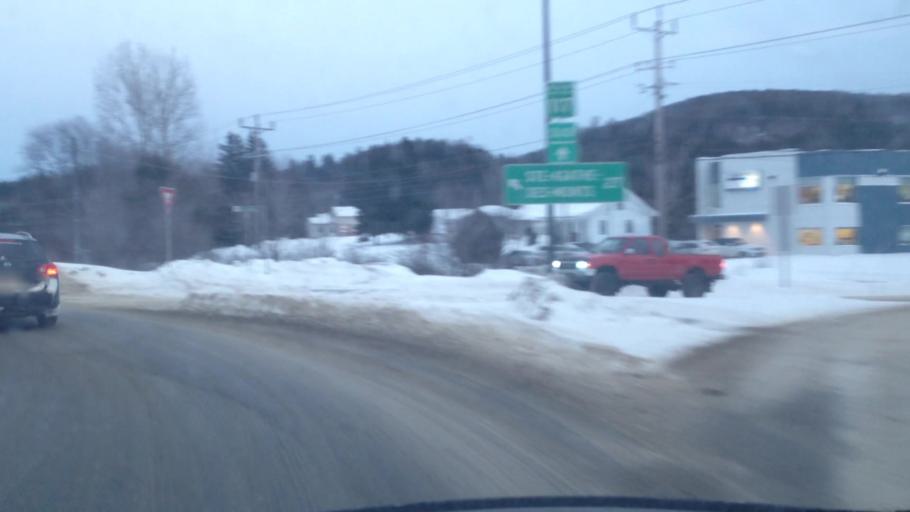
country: CA
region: Quebec
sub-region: Laurentides
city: Mont-Tremblant
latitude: 46.1167
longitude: -74.5630
